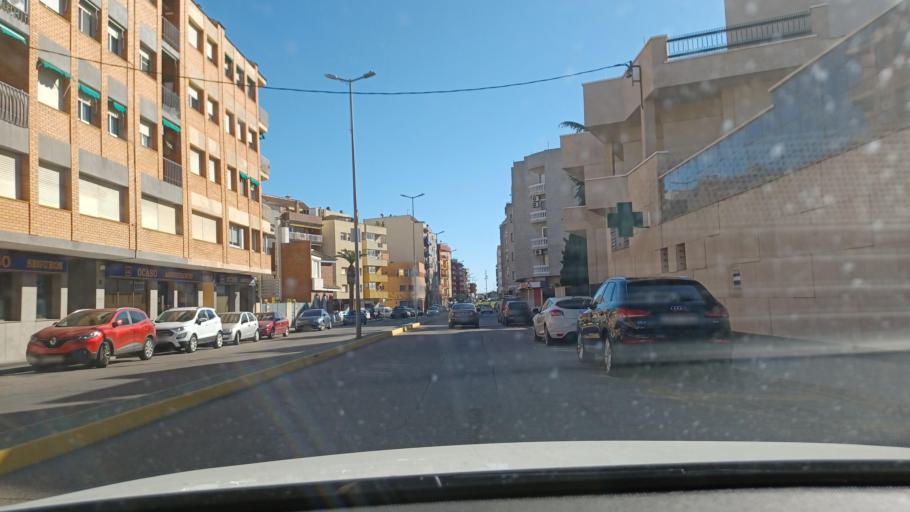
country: ES
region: Catalonia
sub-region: Provincia de Tarragona
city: Amposta
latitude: 40.7059
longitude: 0.5780
